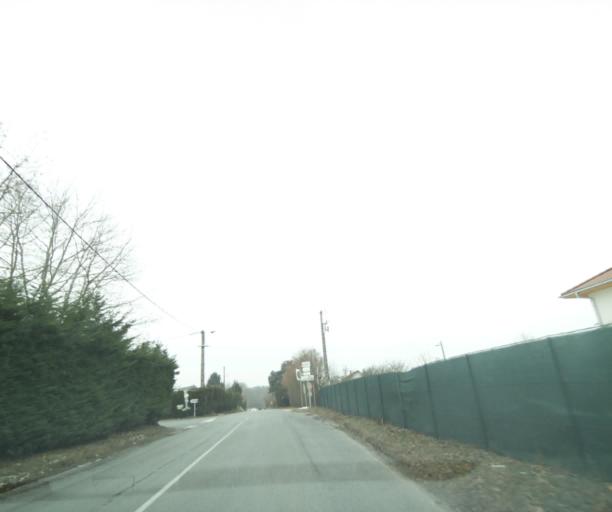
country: FR
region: Rhone-Alpes
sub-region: Departement de la Haute-Savoie
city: Arenthon
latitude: 46.1229
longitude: 6.3118
